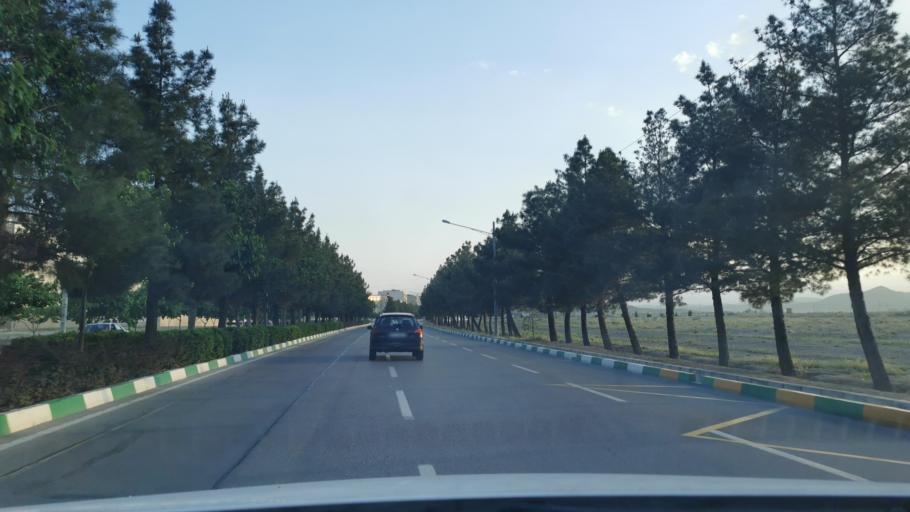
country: IR
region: Razavi Khorasan
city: Torqabeh
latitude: 36.3825
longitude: 59.4624
